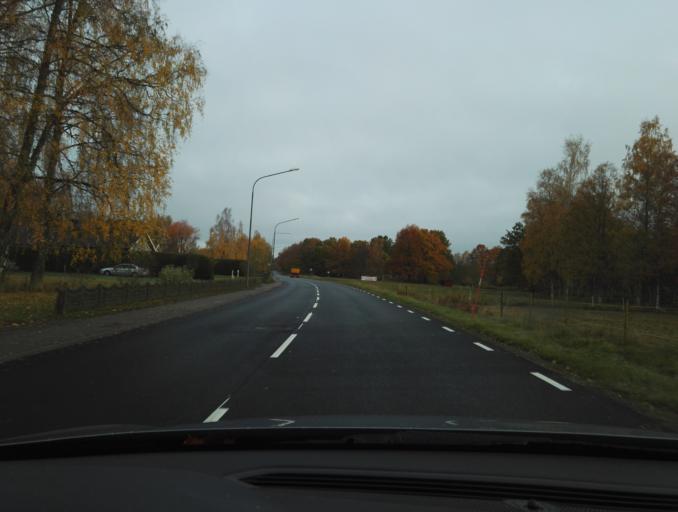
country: SE
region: Kronoberg
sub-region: Vaxjo Kommun
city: Rottne
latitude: 57.0203
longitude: 14.7780
